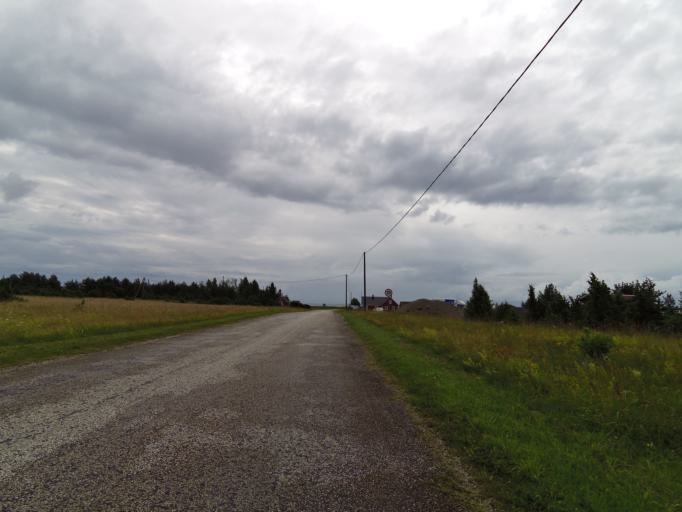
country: EE
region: Laeaene
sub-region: Vormsi vald
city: Hullo
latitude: 58.9746
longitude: 23.3123
